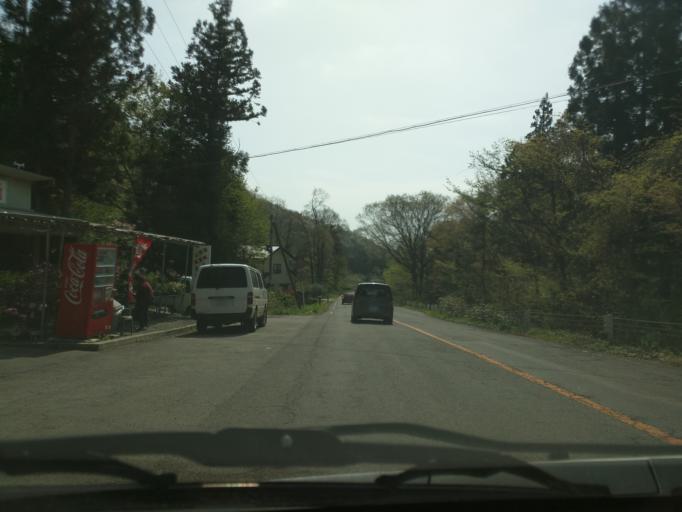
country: JP
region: Fukushima
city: Nihommatsu
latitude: 37.6023
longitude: 140.3735
